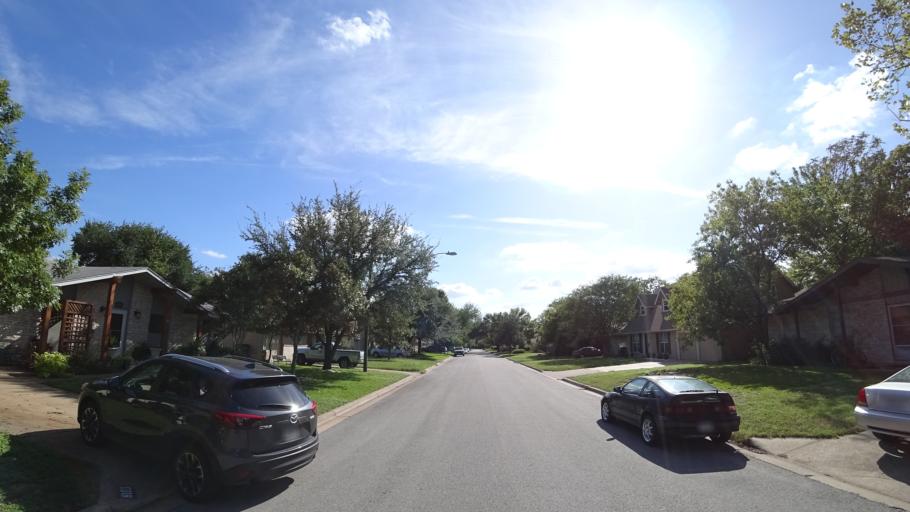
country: US
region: Texas
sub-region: Williamson County
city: Jollyville
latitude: 30.3628
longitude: -97.7341
